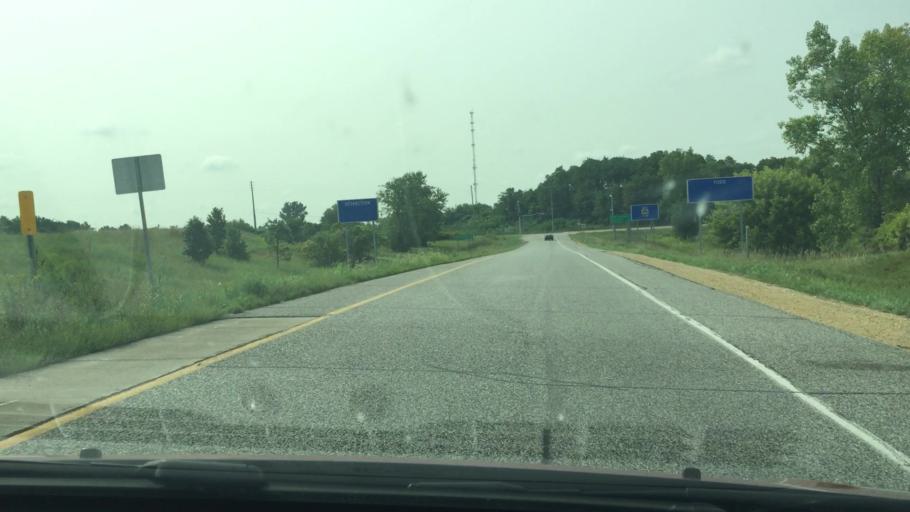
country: US
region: Iowa
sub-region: Scott County
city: Buffalo
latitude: 41.5116
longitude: -90.6742
